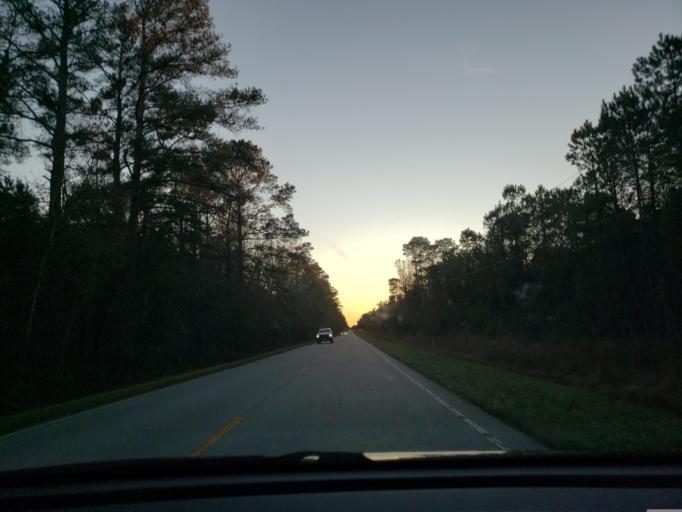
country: US
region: North Carolina
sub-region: Onslow County
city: Jacksonville
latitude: 34.7224
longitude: -77.6115
